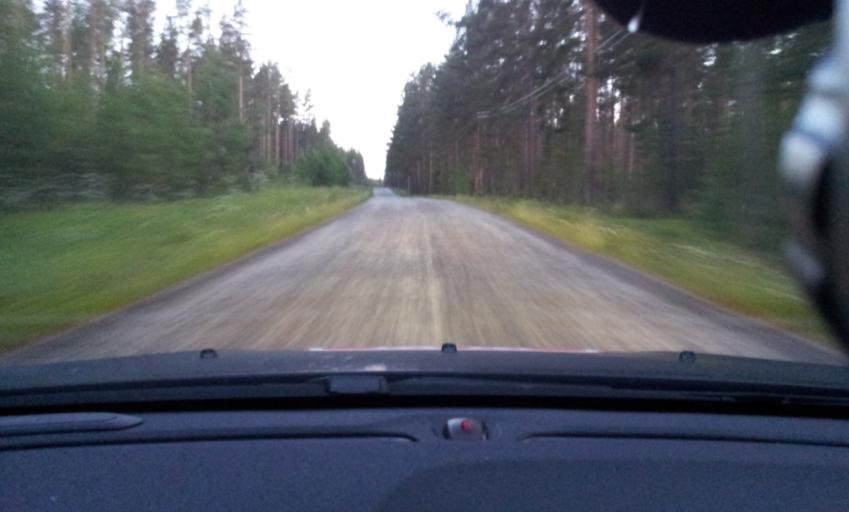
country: SE
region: Vaesternorrland
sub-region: Ange Kommun
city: Fransta
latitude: 62.7828
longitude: 16.0609
